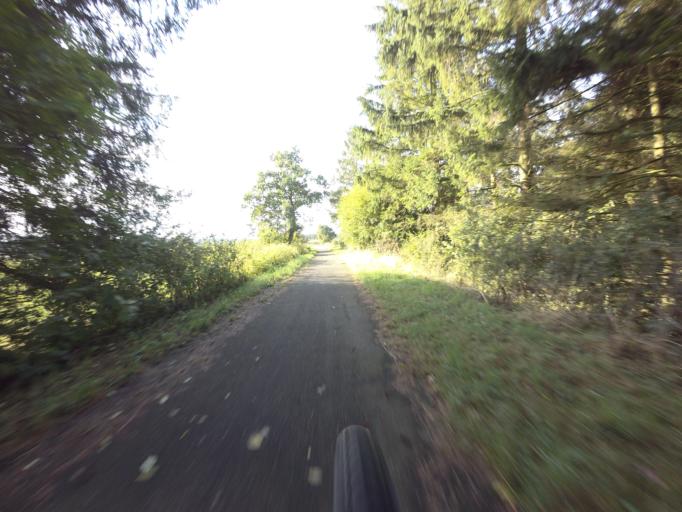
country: DK
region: Central Jutland
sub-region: Viborg Kommune
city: Bjerringbro
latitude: 56.4583
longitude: 9.5850
